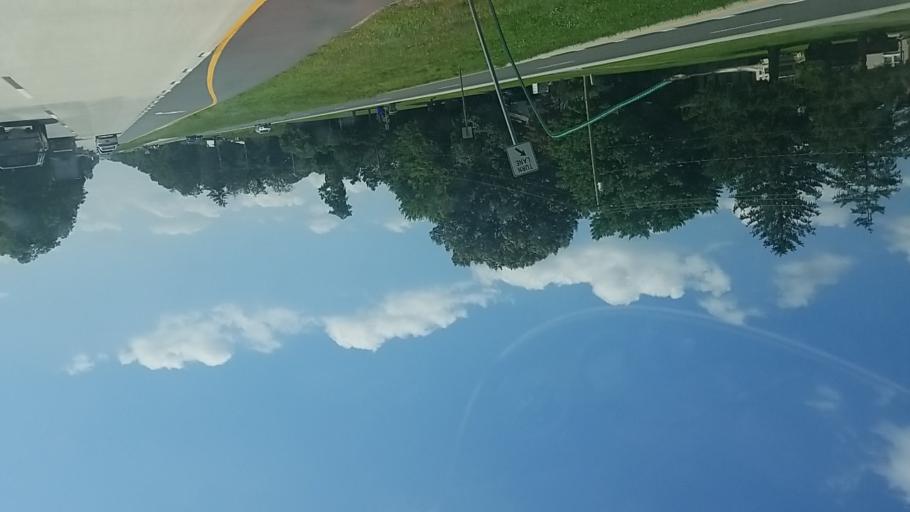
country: US
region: Delaware
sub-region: Sussex County
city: Milford
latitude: 38.8493
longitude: -75.4393
